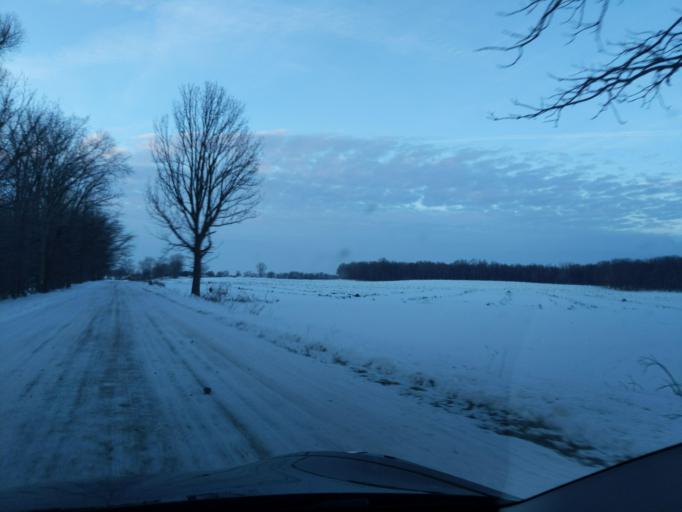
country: US
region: Michigan
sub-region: Ingham County
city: Williamston
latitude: 42.5647
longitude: -84.3090
